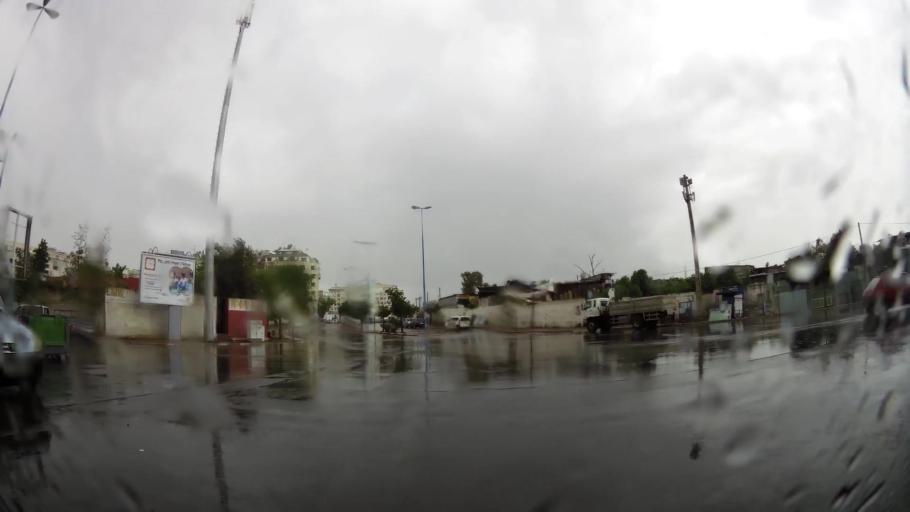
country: MA
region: Grand Casablanca
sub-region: Casablanca
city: Casablanca
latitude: 33.5718
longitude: -7.6290
